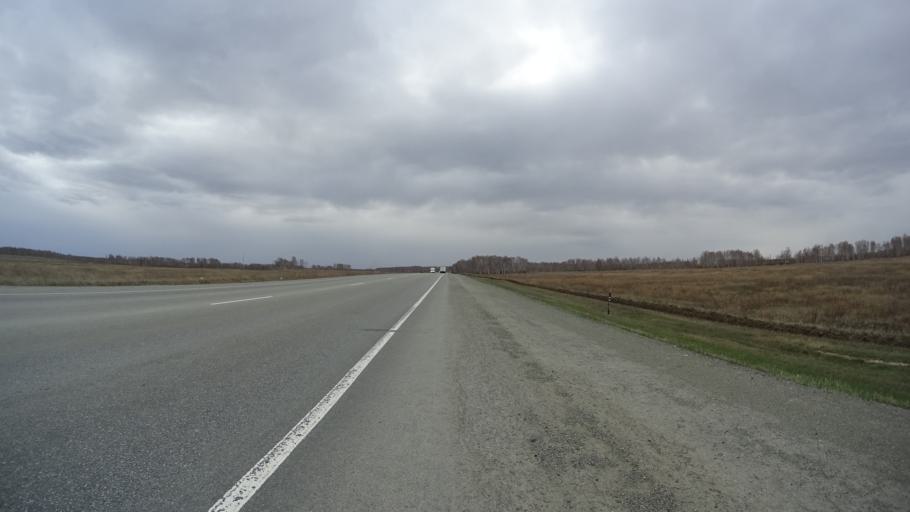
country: RU
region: Chelyabinsk
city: Yemanzhelinsk
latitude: 54.7029
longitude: 61.2543
